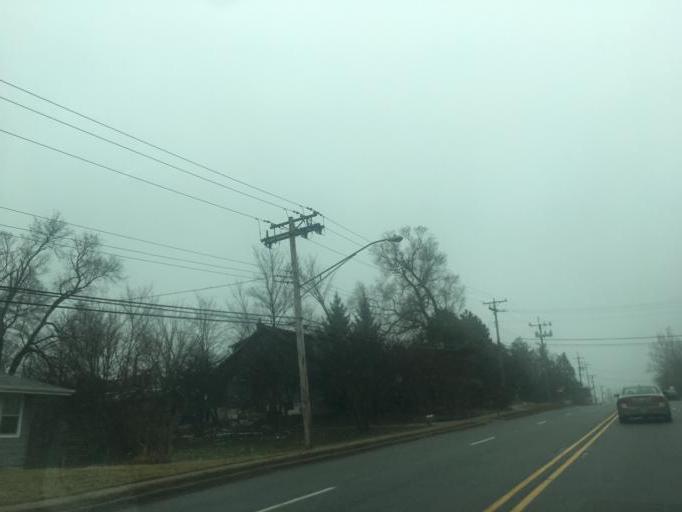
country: US
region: Illinois
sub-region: DuPage County
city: Downers Grove
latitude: 41.7892
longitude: -88.0377
